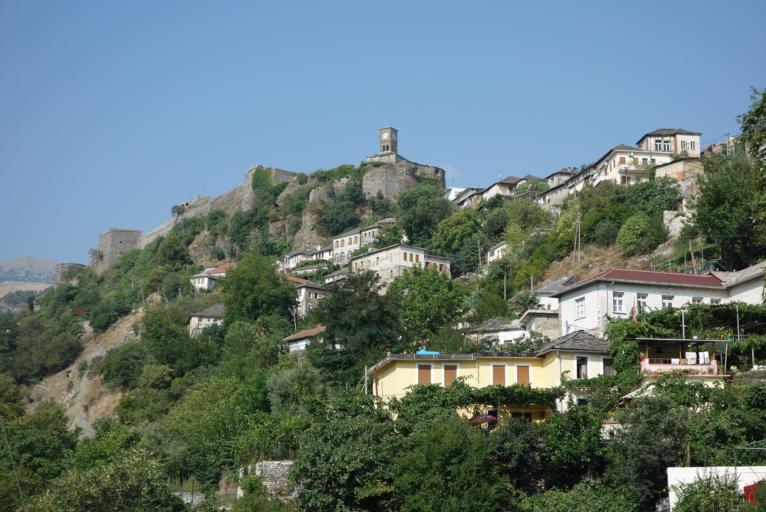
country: AL
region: Gjirokaster
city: Gjirokaster
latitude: 40.0761
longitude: 20.1465
